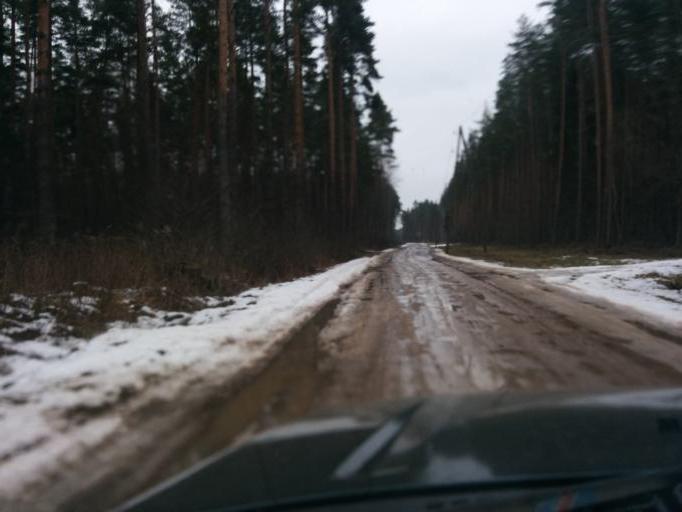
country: LV
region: Ozolnieku
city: Ozolnieki
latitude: 56.6770
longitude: 23.7595
